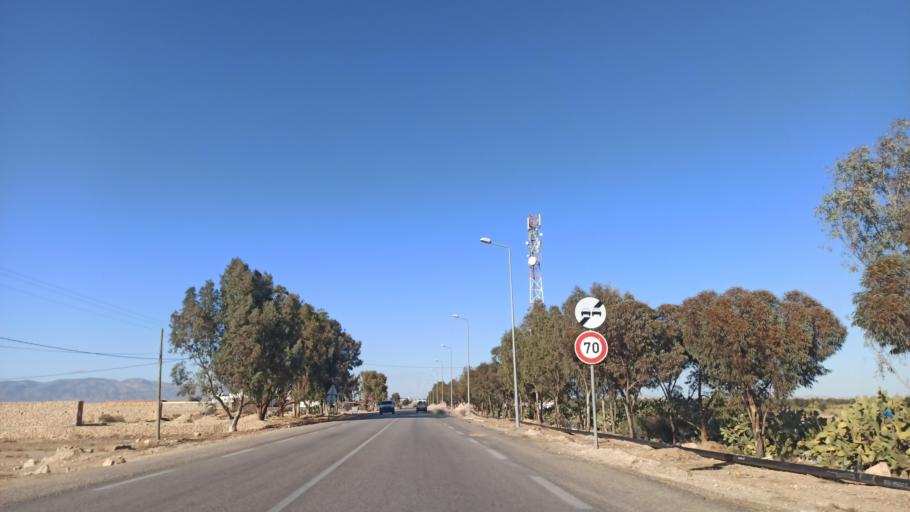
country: TN
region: Sidi Bu Zayd
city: Jilma
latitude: 35.2910
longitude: 9.4178
